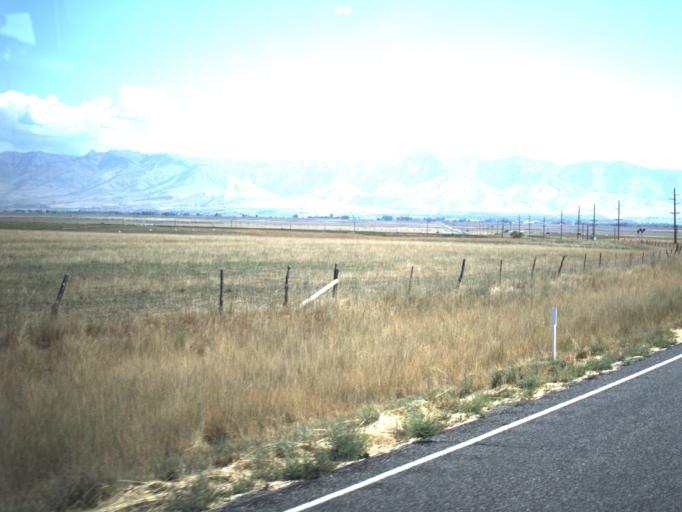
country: US
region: Utah
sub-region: Cache County
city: Benson
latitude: 41.8453
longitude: -111.9648
